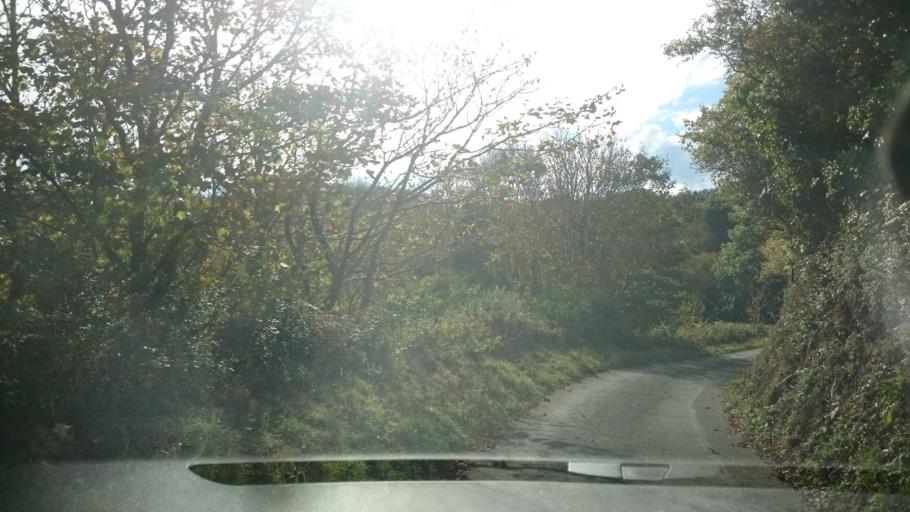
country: GG
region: St Peter Port
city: Saint Peter Port
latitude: 49.4320
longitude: -2.6629
